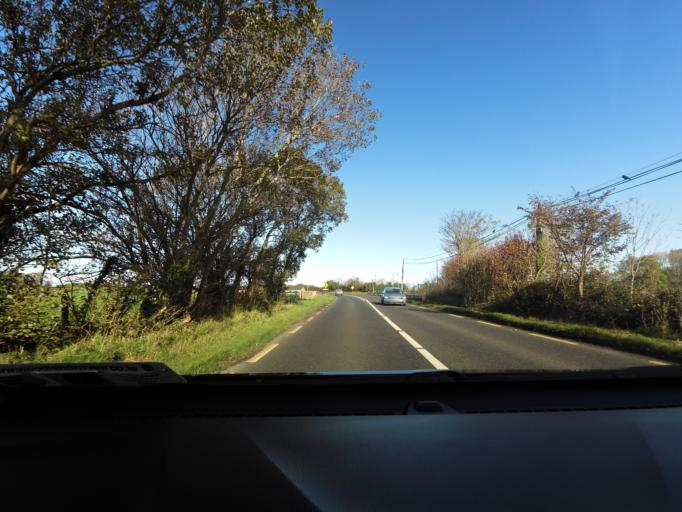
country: IE
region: Connaught
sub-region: County Galway
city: Claregalway
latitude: 53.4227
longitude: -9.0335
